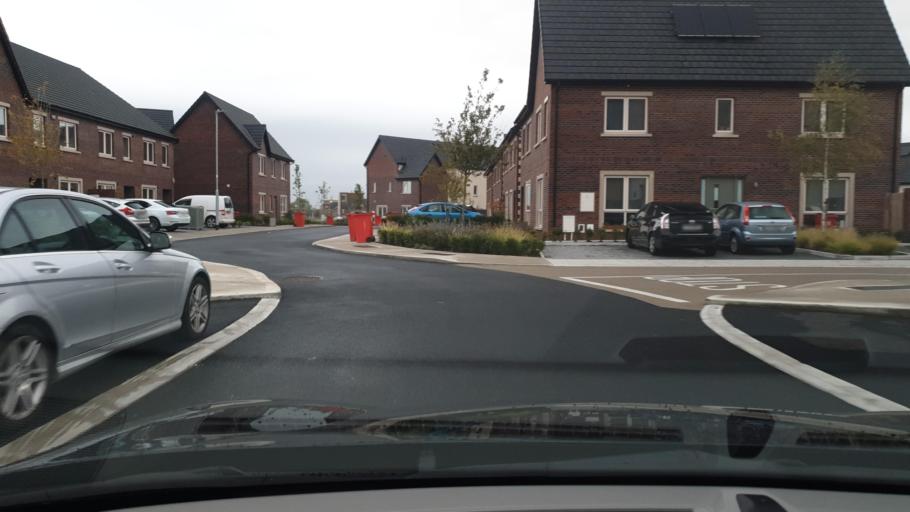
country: IE
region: Leinster
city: Lucan
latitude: 53.3448
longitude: -6.4666
